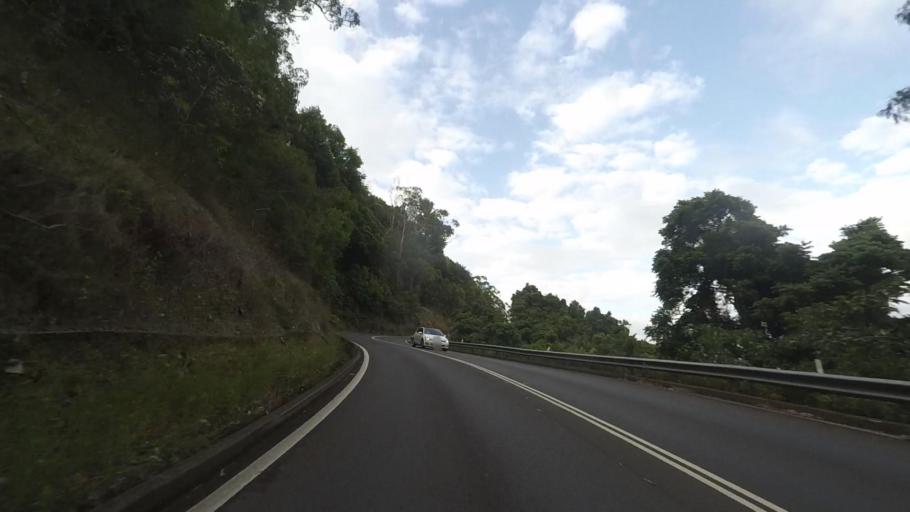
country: AU
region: New South Wales
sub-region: Wollongong
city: Bulli
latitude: -34.3143
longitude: 150.8956
